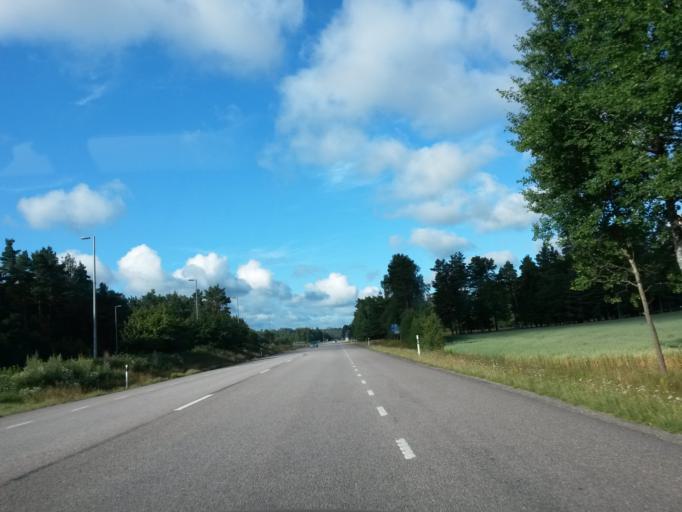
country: SE
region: Vaestra Goetaland
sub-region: Vargarda Kommun
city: Jonstorp
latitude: 57.9846
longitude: 12.6911
